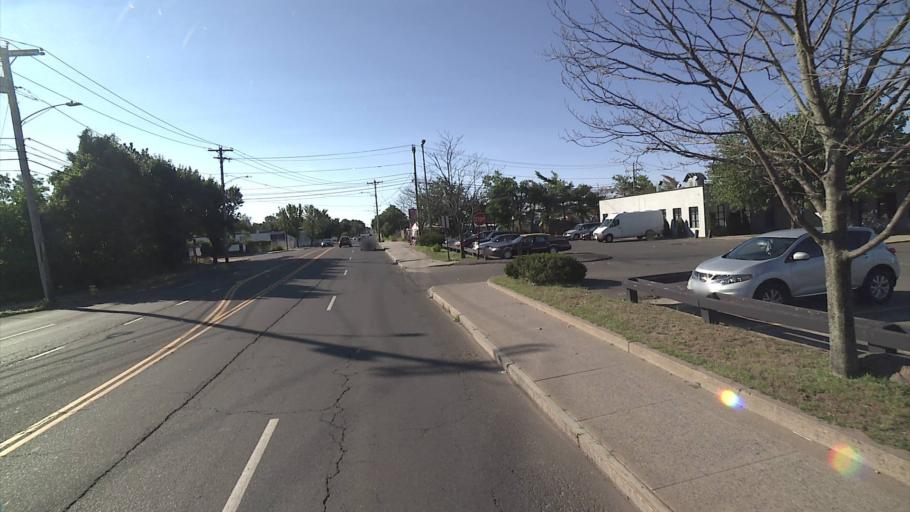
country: US
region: Connecticut
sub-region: New Haven County
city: New Haven
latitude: 41.2943
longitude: -72.9454
